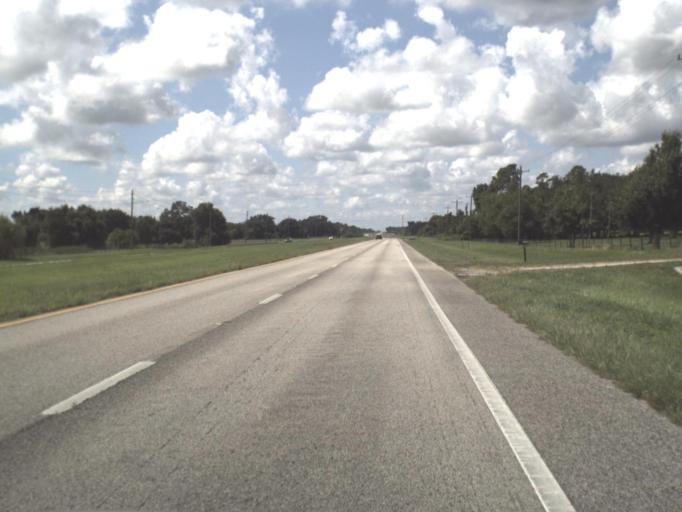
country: US
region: Florida
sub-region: DeSoto County
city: Arcadia
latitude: 27.3283
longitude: -81.8111
